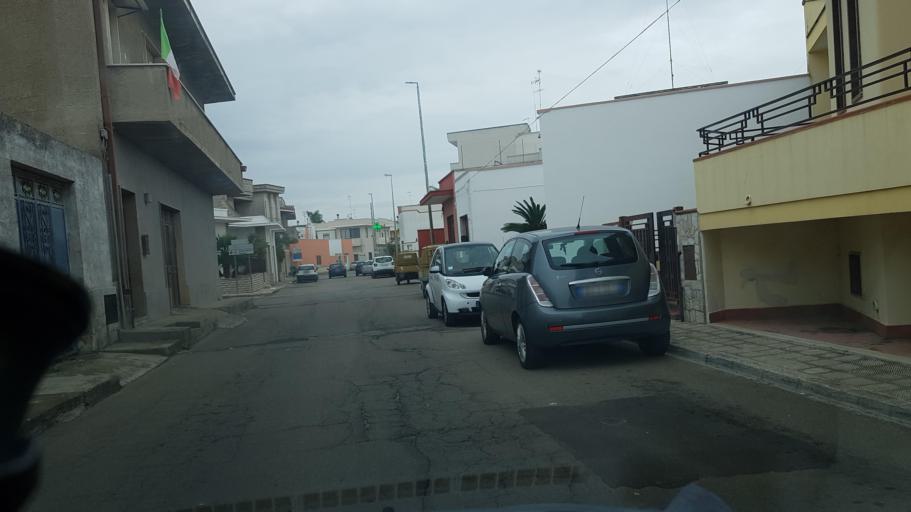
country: IT
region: Apulia
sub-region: Provincia di Lecce
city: Veglie
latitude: 40.3401
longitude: 17.9674
